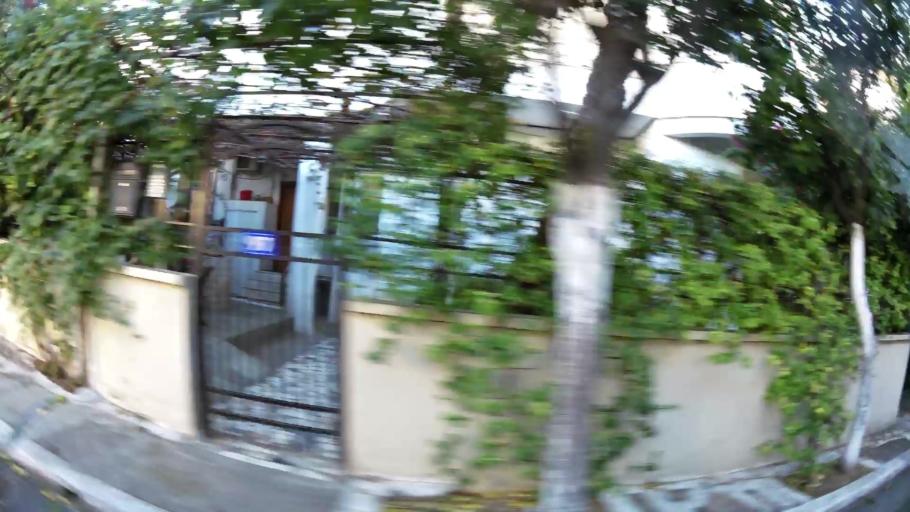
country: GR
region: Attica
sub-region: Nomarchia Athinas
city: Khalandrion
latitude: 38.0135
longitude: 23.7983
